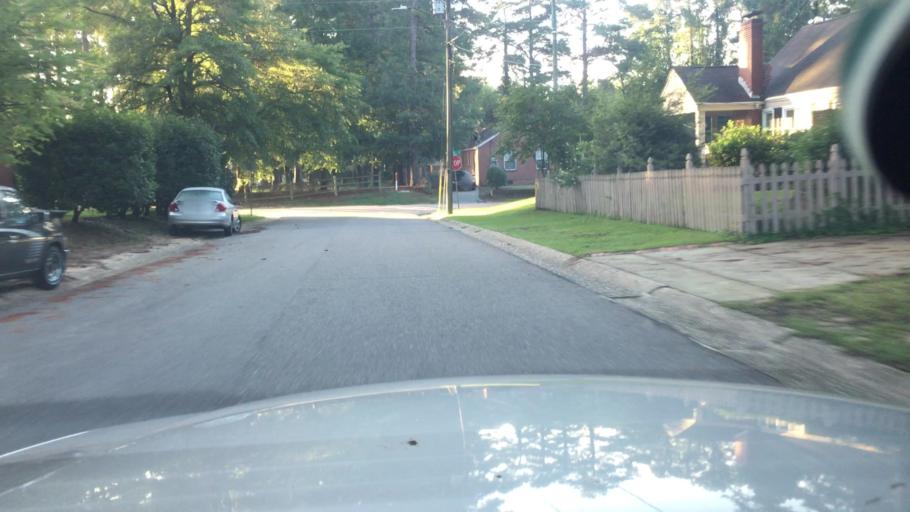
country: US
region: North Carolina
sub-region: Cumberland County
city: Fayetteville
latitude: 35.0616
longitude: -78.9140
